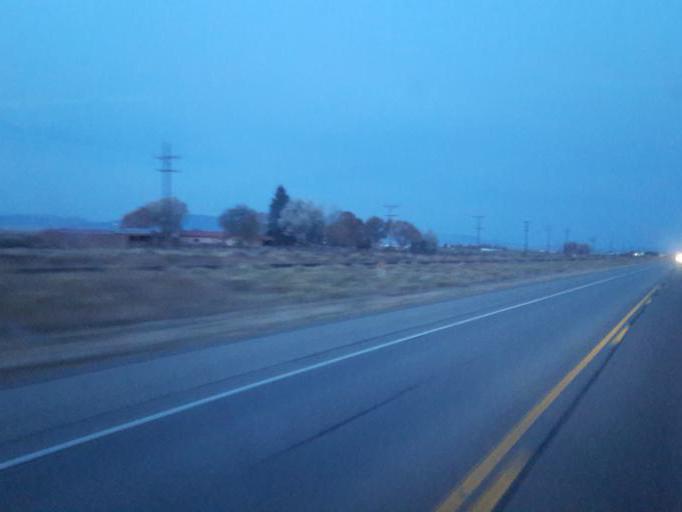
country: US
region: Colorado
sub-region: Alamosa County
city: Alamosa
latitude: 37.4935
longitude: -105.9377
